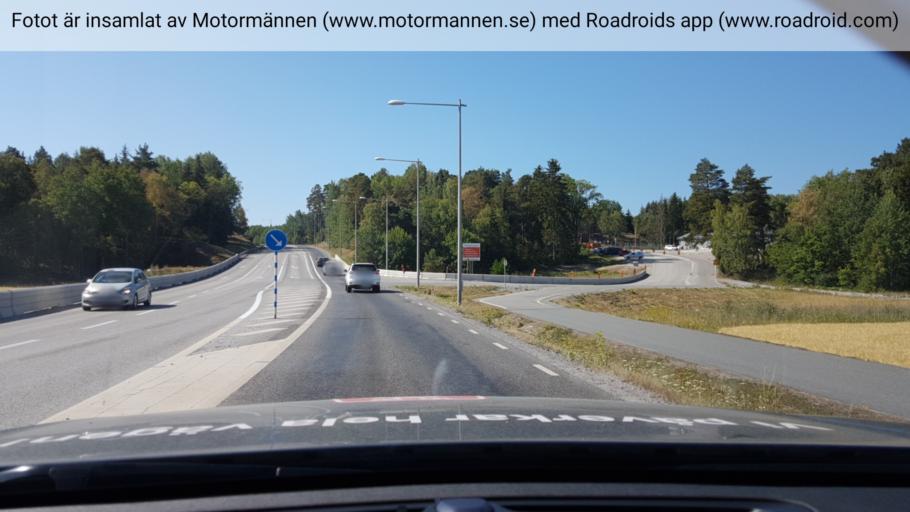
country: SE
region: Stockholm
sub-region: Ekero Kommun
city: Ekeroe
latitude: 59.3154
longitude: 17.8615
